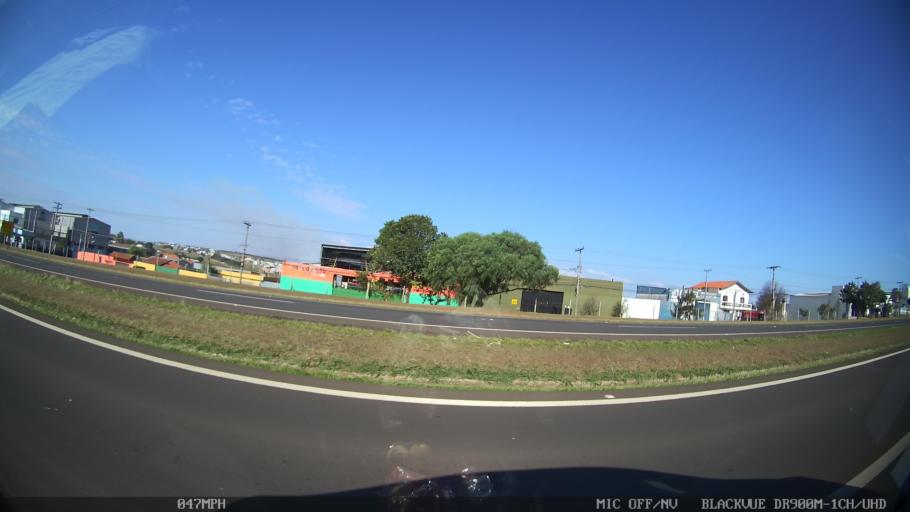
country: BR
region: Sao Paulo
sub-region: Piracicaba
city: Piracicaba
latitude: -22.6837
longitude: -47.6380
